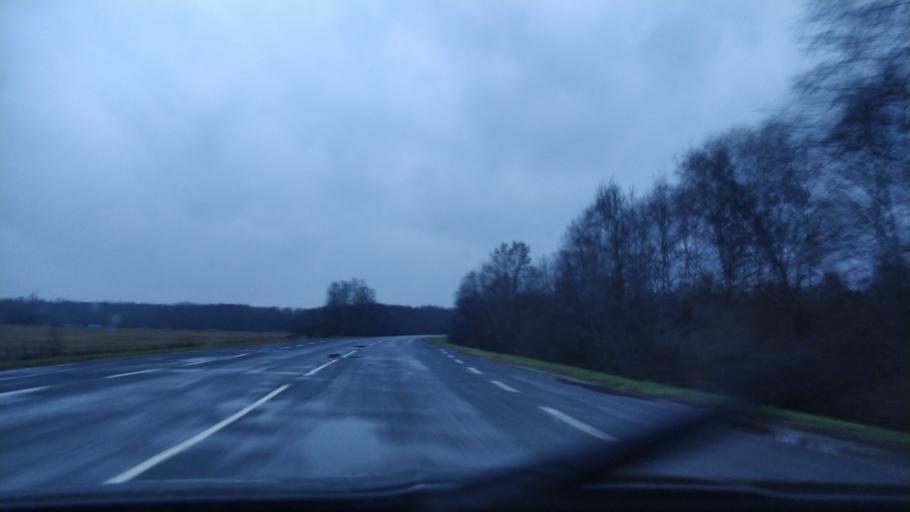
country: EE
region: Laeaene
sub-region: Lihula vald
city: Lihula
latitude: 58.7053
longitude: 23.8622
